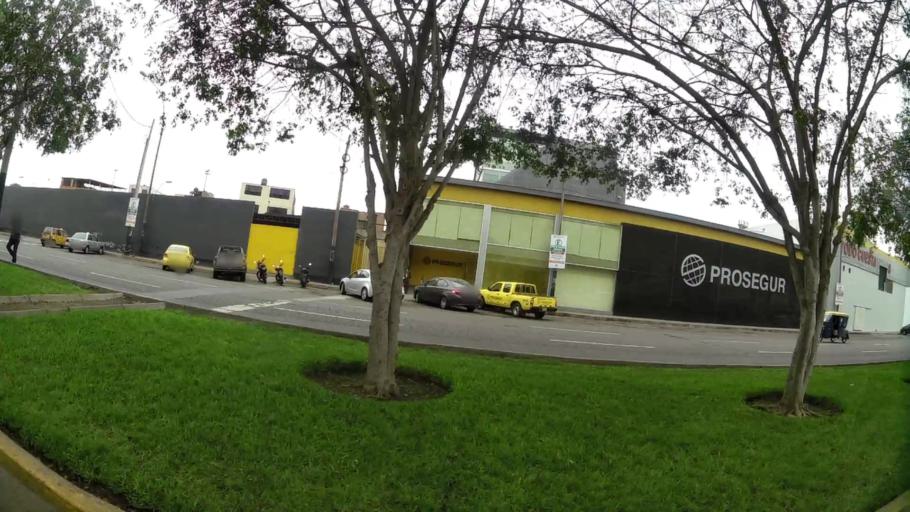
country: PE
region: Lima
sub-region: Lima
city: Surco
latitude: -12.1498
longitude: -76.9873
